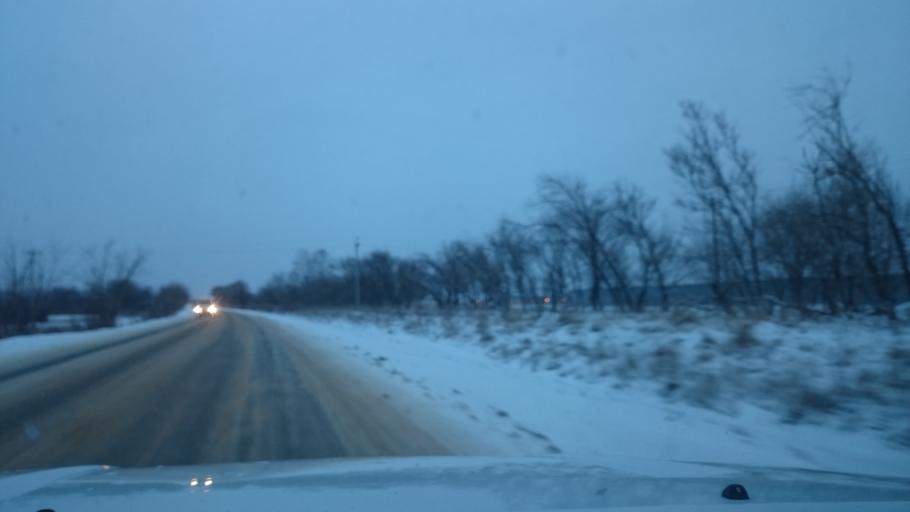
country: RU
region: Tula
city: Leninskiy
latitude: 54.2495
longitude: 37.3334
